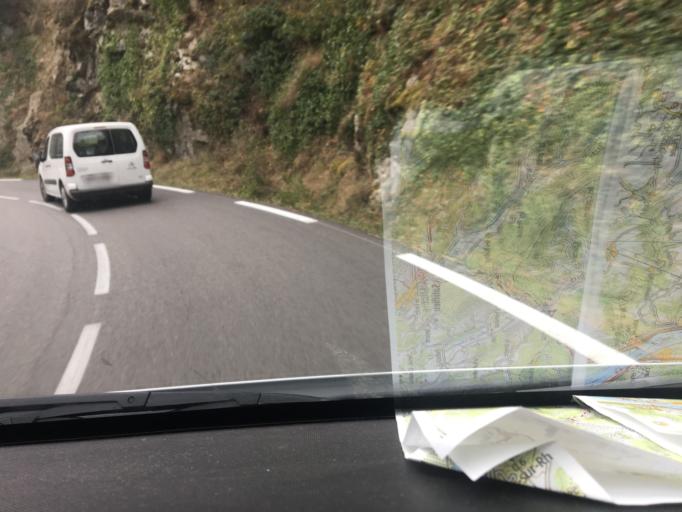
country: FR
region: Rhone-Alpes
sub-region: Departement de l'Ardeche
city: Saint-Jean-de-Muzols
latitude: 45.0657
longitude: 4.7561
